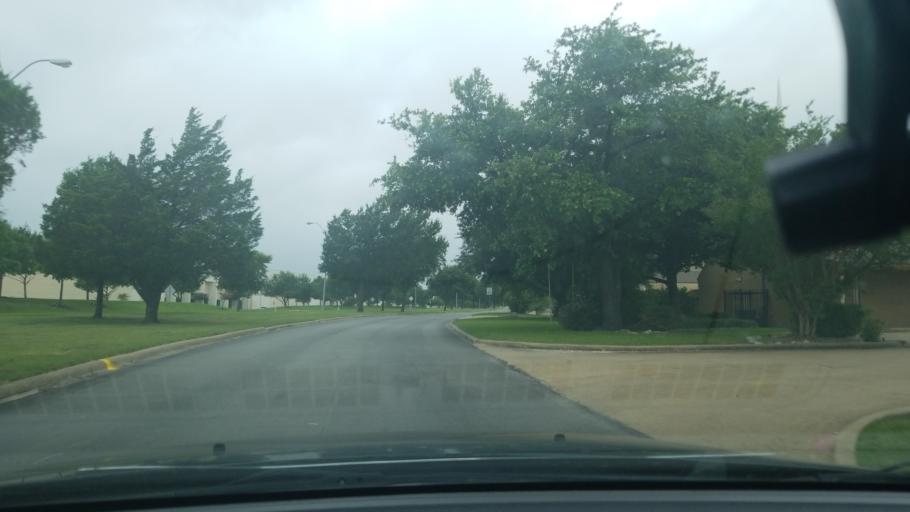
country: US
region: Texas
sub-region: Dallas County
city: Mesquite
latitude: 32.7788
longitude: -96.6304
